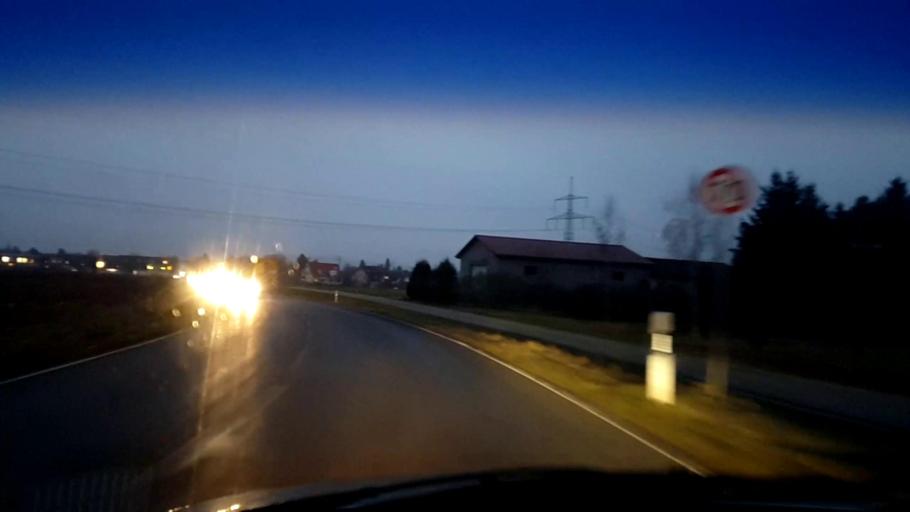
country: DE
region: Bavaria
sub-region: Upper Franconia
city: Hallstadt
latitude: 49.9373
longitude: 10.8831
